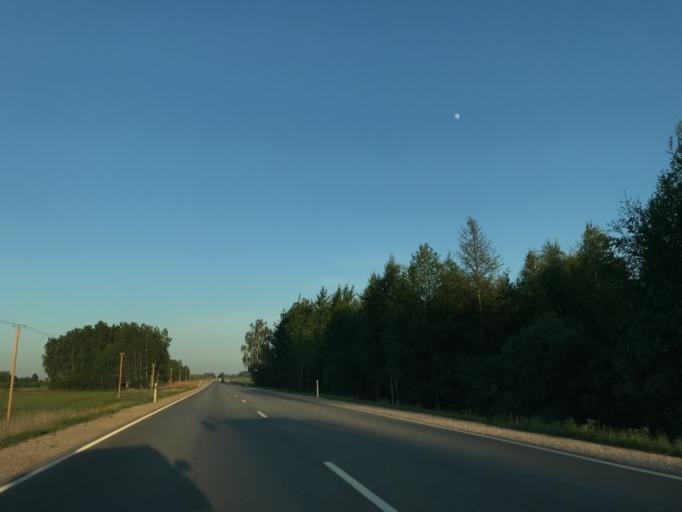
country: LV
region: Vecumnieki
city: Vecumnieki
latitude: 56.5245
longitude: 24.6846
